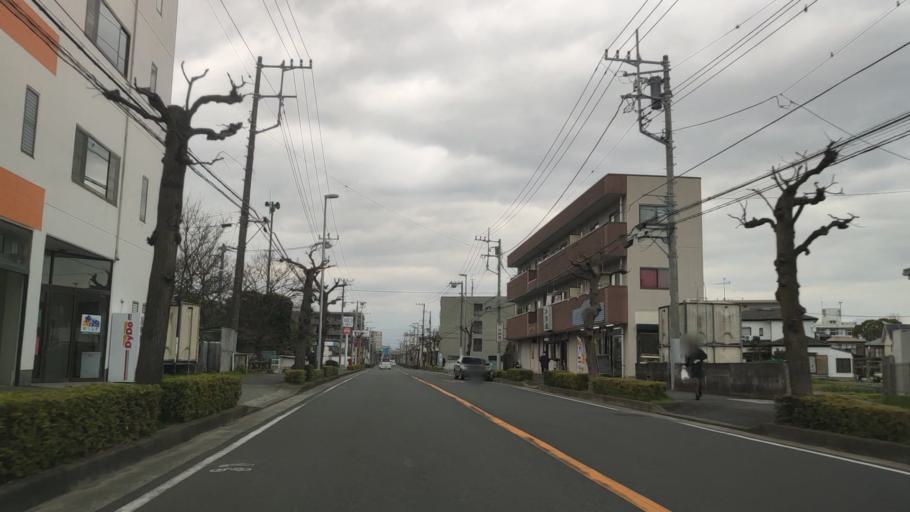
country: JP
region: Kanagawa
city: Odawara
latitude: 35.2683
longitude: 139.1826
